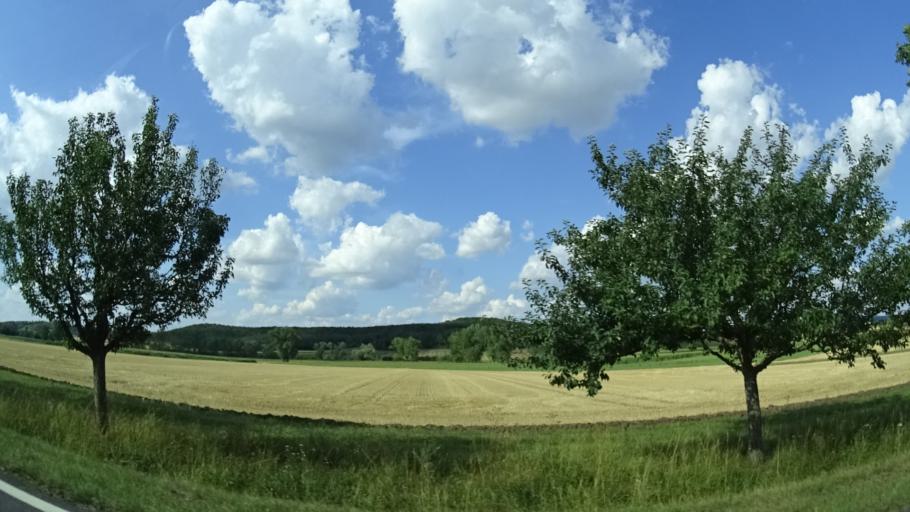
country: DE
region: Bavaria
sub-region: Regierungsbezirk Unterfranken
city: Bad Konigshofen im Grabfeld
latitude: 50.2791
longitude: 10.5214
